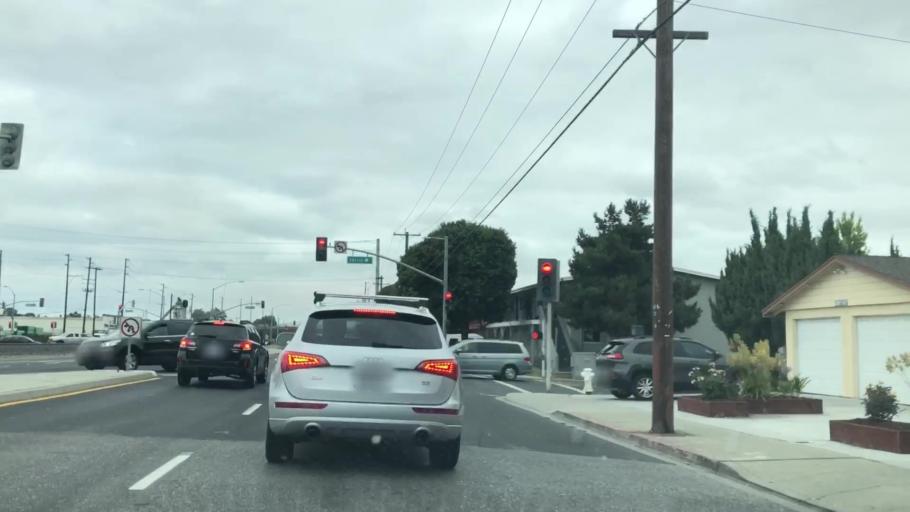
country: US
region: California
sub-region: Santa Clara County
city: Santa Clara
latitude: 37.3852
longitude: -121.9521
